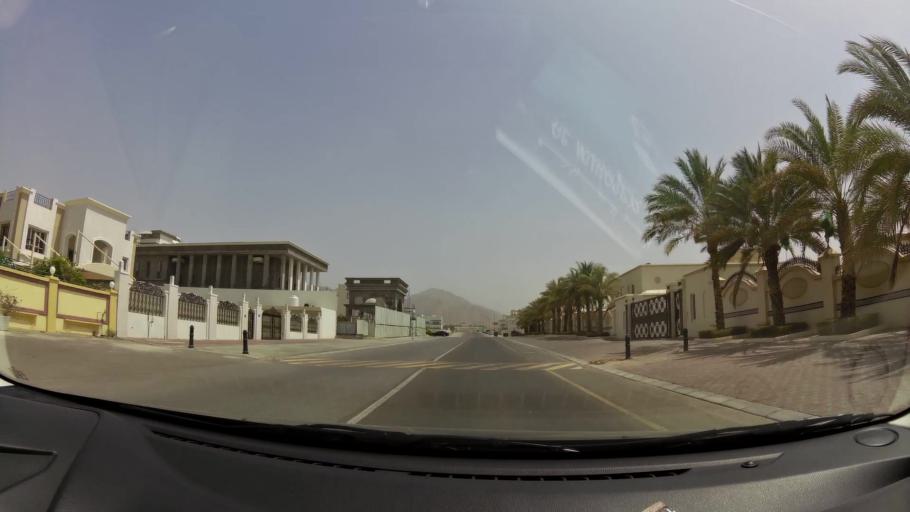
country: OM
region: Muhafazat Masqat
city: Bawshar
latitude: 23.5594
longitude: 58.3943
